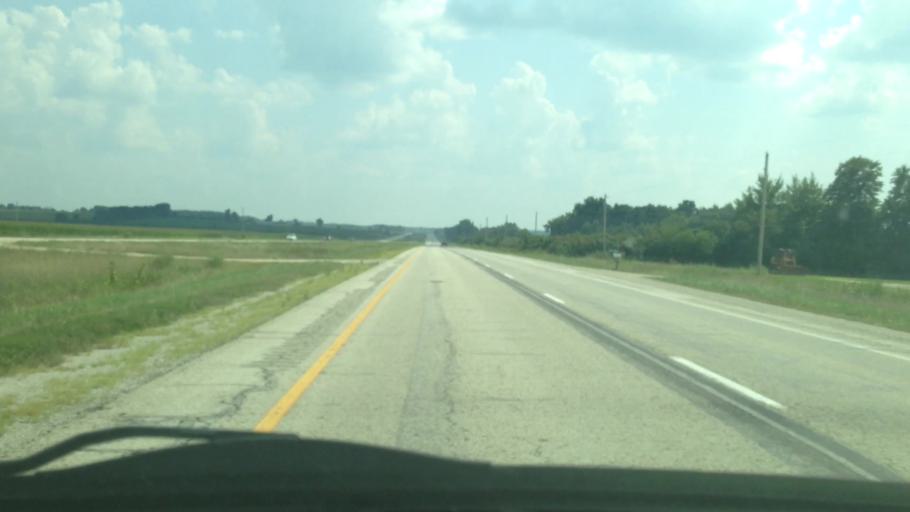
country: US
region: Iowa
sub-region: Chickasaw County
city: New Hampton
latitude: 42.9301
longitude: -92.3176
